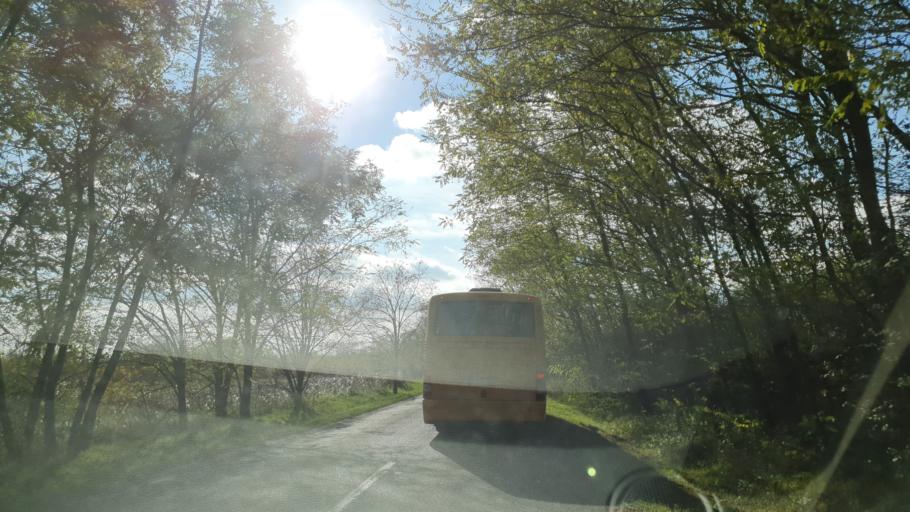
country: HU
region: Szabolcs-Szatmar-Bereg
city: Gyulahaza
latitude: 48.1258
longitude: 22.0885
